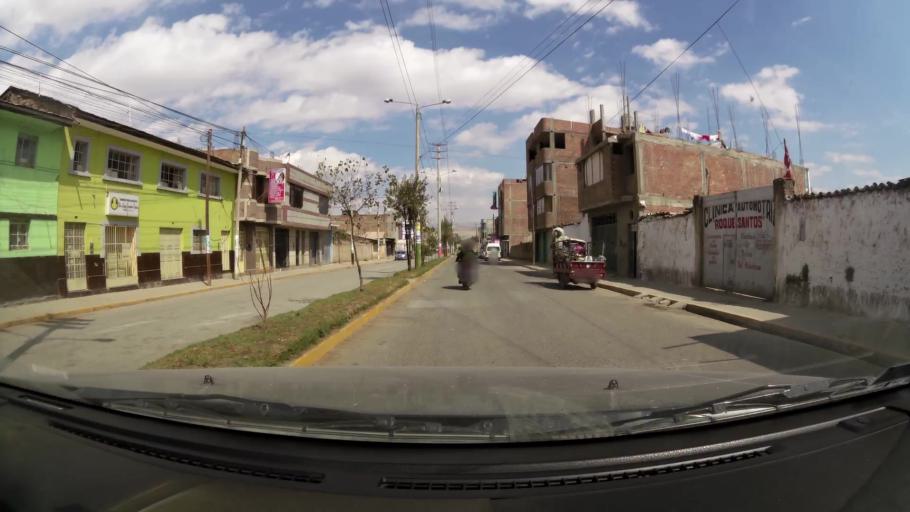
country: PE
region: Junin
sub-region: Provincia de Huancayo
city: El Tambo
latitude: -12.0882
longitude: -75.2082
